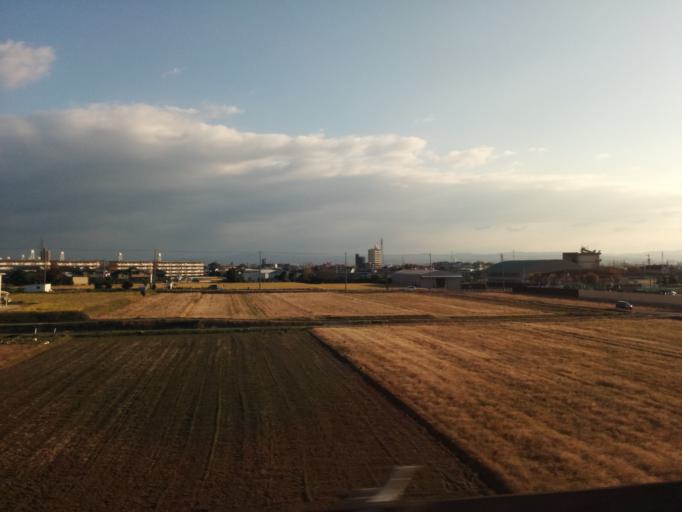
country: JP
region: Aichi
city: Anjo
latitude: 34.9427
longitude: 137.0846
